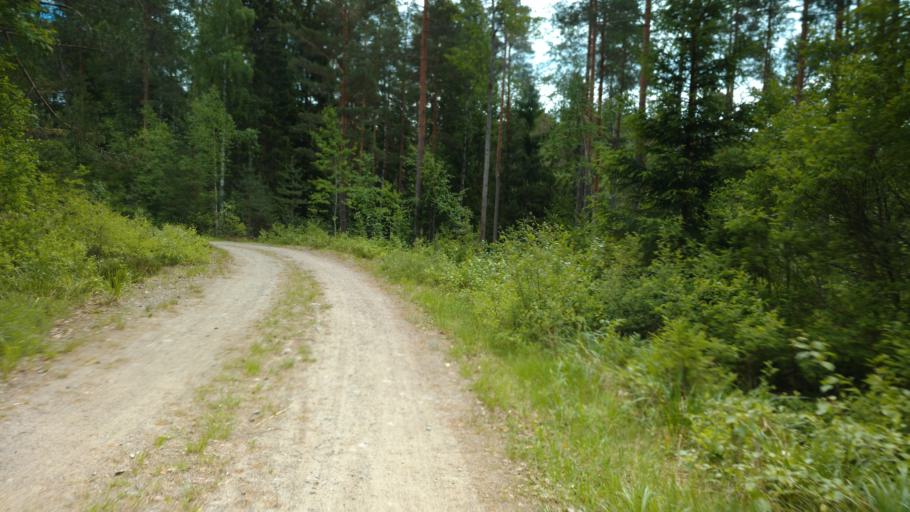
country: FI
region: Uusimaa
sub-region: Raaseporin
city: Pohja
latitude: 60.1135
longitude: 23.5547
